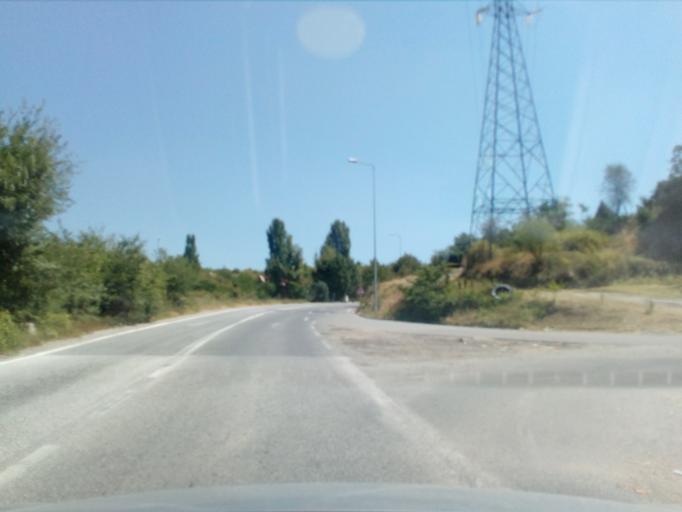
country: MK
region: Veles
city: Veles
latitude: 41.7267
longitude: 21.7882
